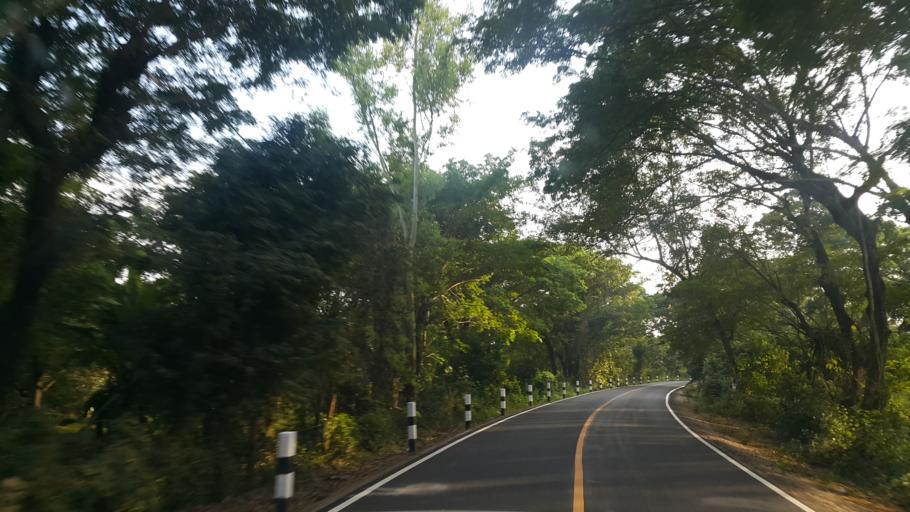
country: TH
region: Lampang
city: Sop Prap
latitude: 17.9359
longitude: 99.3404
